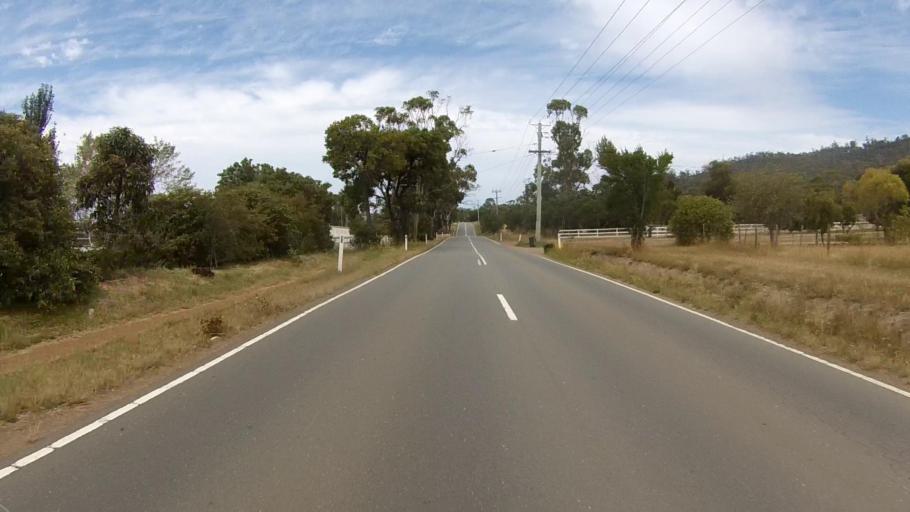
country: AU
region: Tasmania
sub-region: Clarence
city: Acton Park
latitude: -42.8894
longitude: 147.4827
